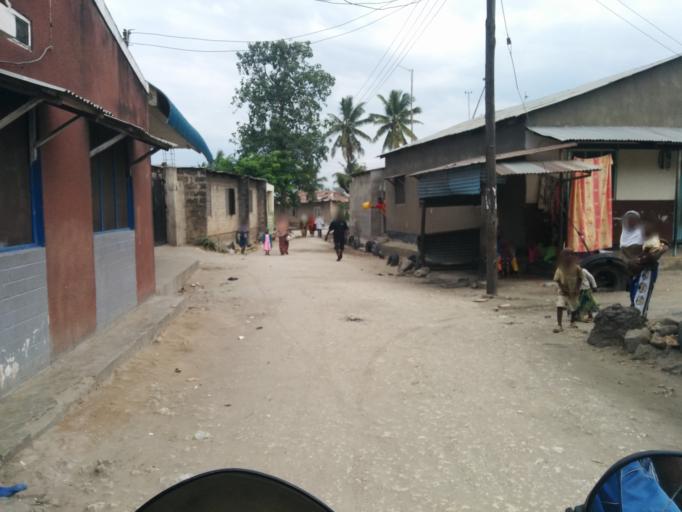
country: TZ
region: Dar es Salaam
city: Dar es Salaam
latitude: -6.8613
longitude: 39.2494
